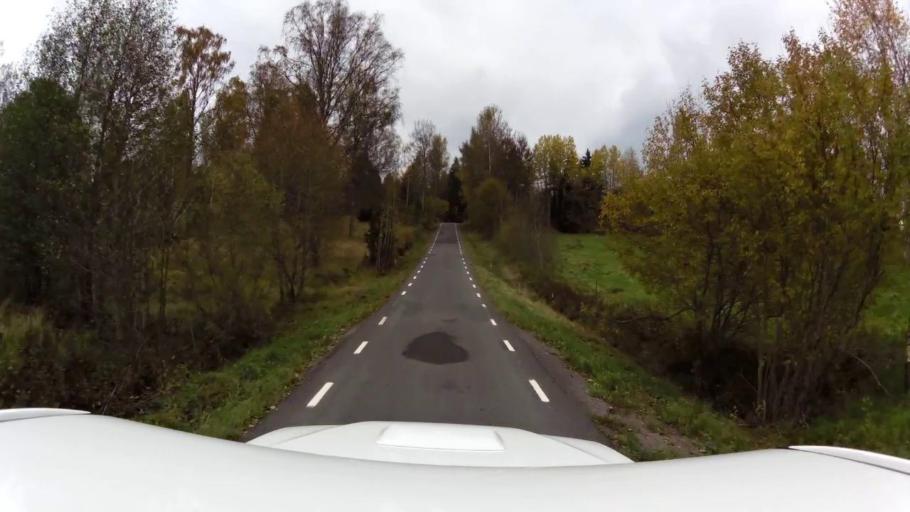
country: SE
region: OEstergoetland
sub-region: Linkopings Kommun
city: Ljungsbro
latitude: 58.5749
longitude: 15.4619
